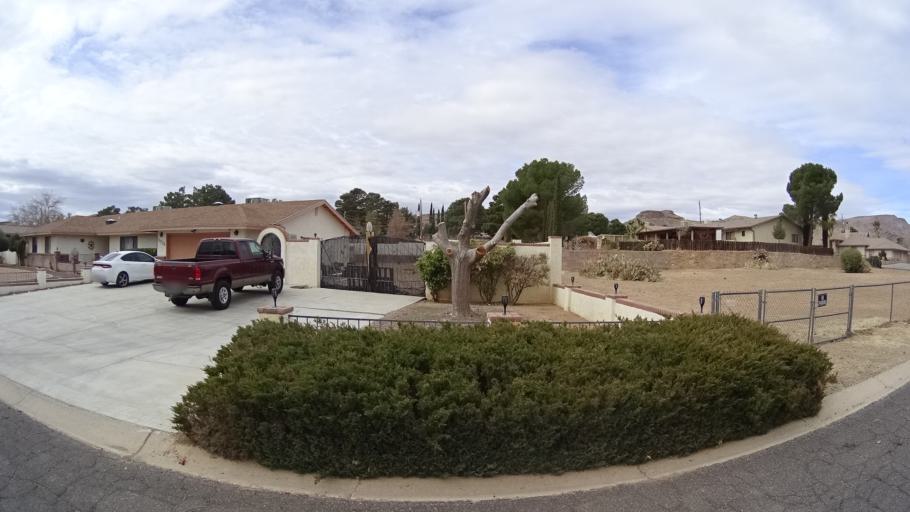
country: US
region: Arizona
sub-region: Mohave County
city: New Kingman-Butler
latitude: 35.2358
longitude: -114.0443
